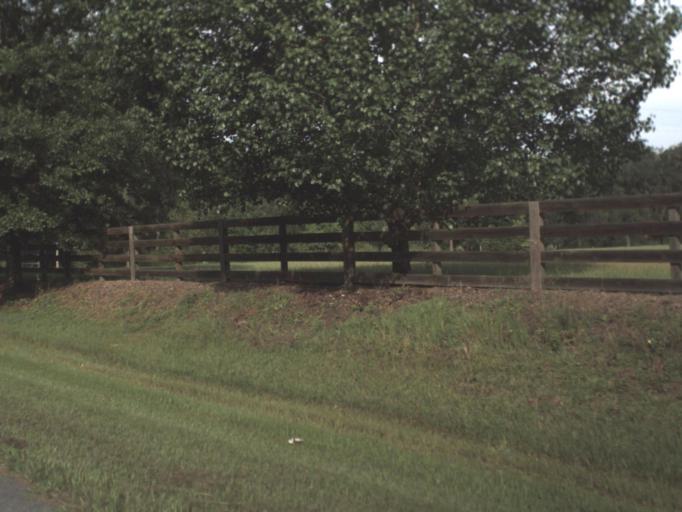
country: US
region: Florida
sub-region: Madison County
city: Madison
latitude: 30.4236
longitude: -83.6322
